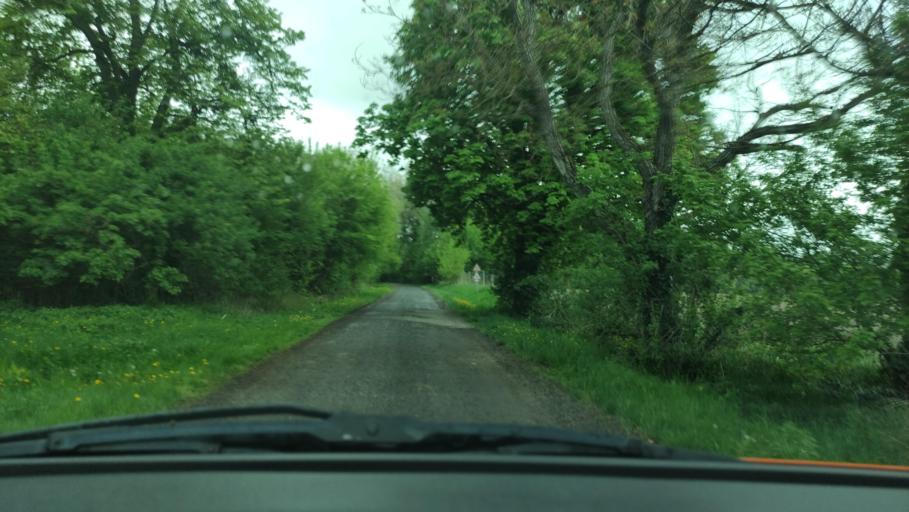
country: HR
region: Osjecko-Baranjska
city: Batina
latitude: 45.9084
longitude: 18.7587
